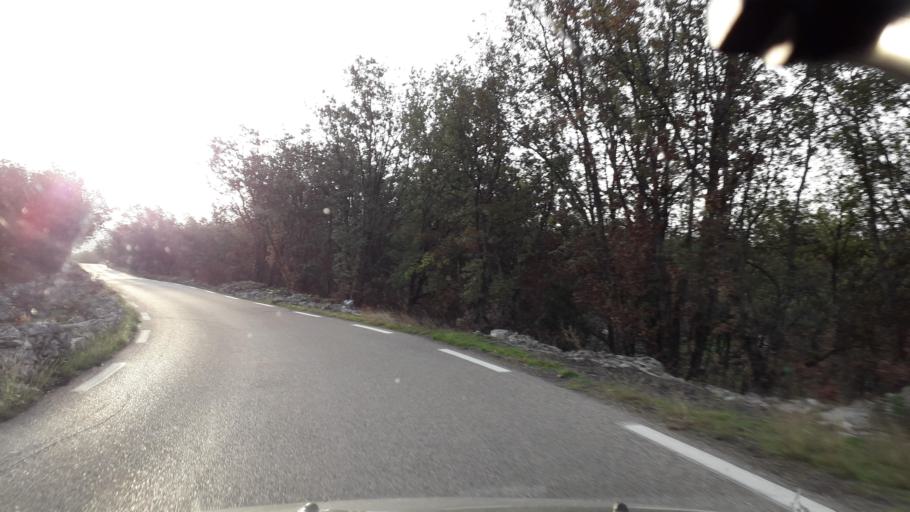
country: FR
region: Rhone-Alpes
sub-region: Departement de l'Ardeche
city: Saint-Privat
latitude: 44.6107
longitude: 4.4460
